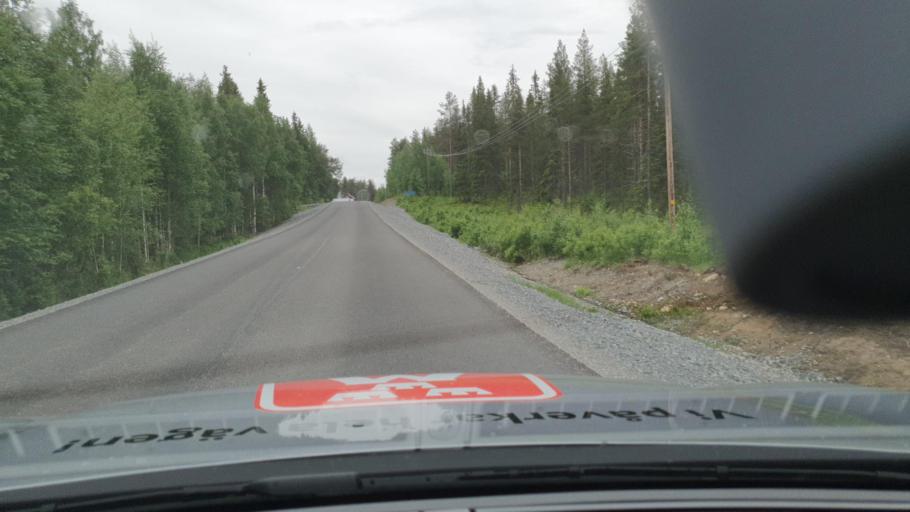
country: SE
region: Norrbotten
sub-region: Overtornea Kommun
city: OEvertornea
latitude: 66.6209
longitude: 23.2867
